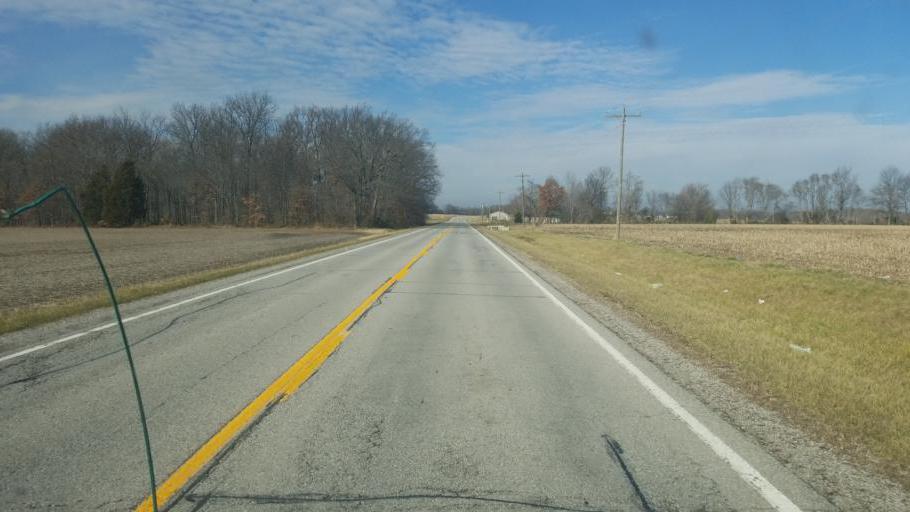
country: US
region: Illinois
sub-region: Saline County
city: Eldorado
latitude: 37.9098
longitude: -88.4542
